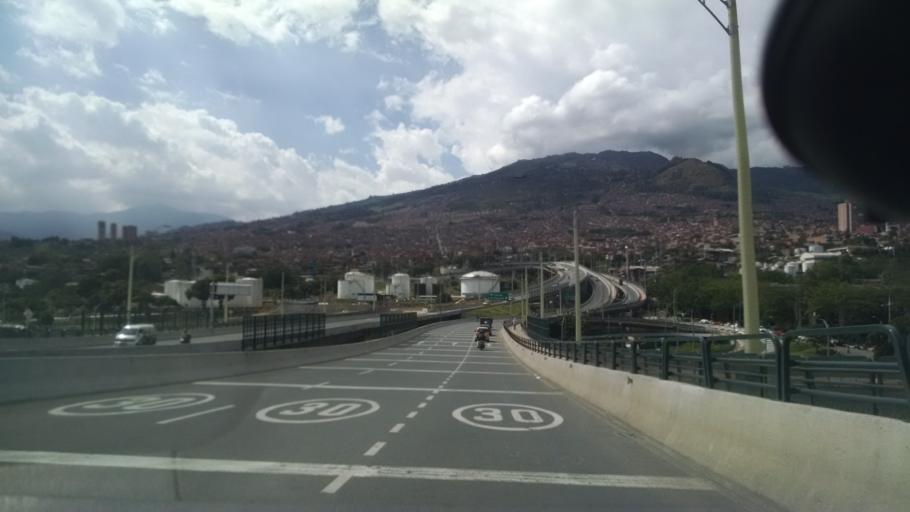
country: CO
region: Antioquia
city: Medellin
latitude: 6.2861
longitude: -75.5655
